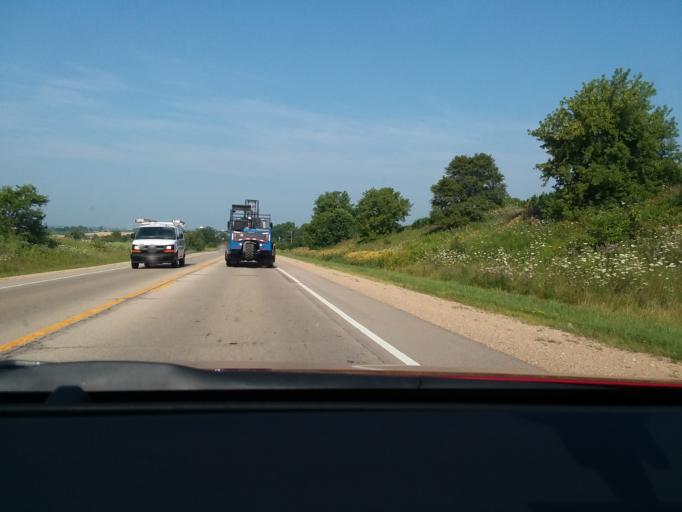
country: US
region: Wisconsin
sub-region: Dane County
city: Waunakee
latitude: 43.1921
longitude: -89.3977
